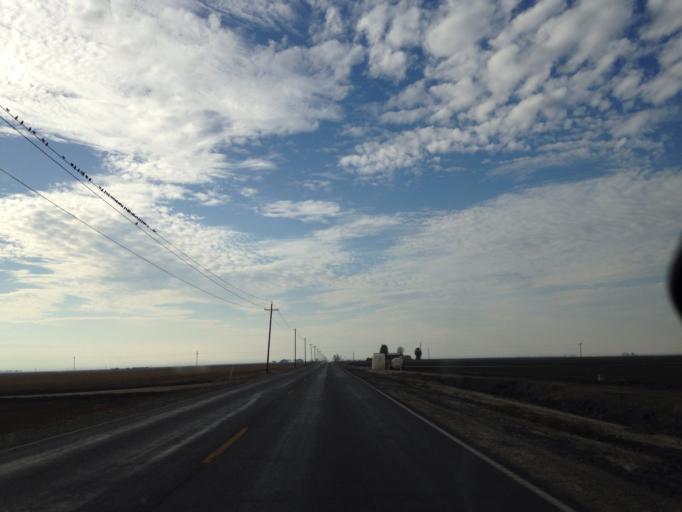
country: US
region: California
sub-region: Kern County
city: Buttonwillow
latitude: 35.4422
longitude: -119.5124
